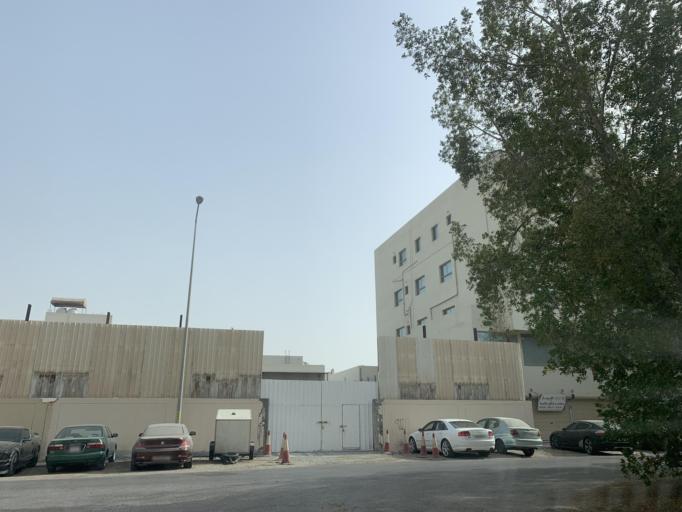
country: BH
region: Northern
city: Madinat `Isa
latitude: 26.1770
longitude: 50.5260
